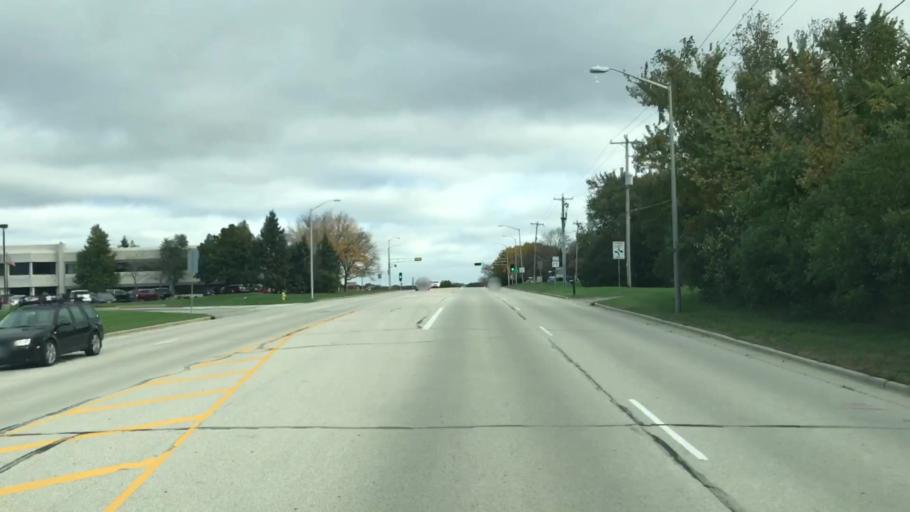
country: US
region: Wisconsin
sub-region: Waukesha County
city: Waukesha
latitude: 43.0306
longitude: -88.2258
